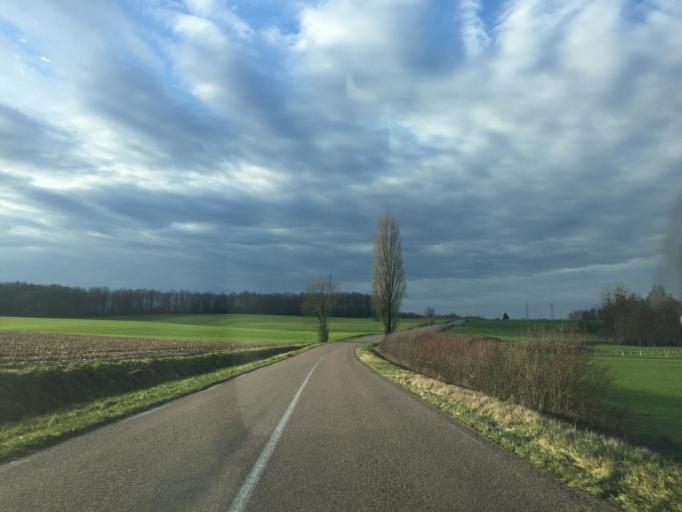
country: FR
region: Franche-Comte
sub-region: Departement du Jura
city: Arbois
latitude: 46.9229
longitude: 5.6989
